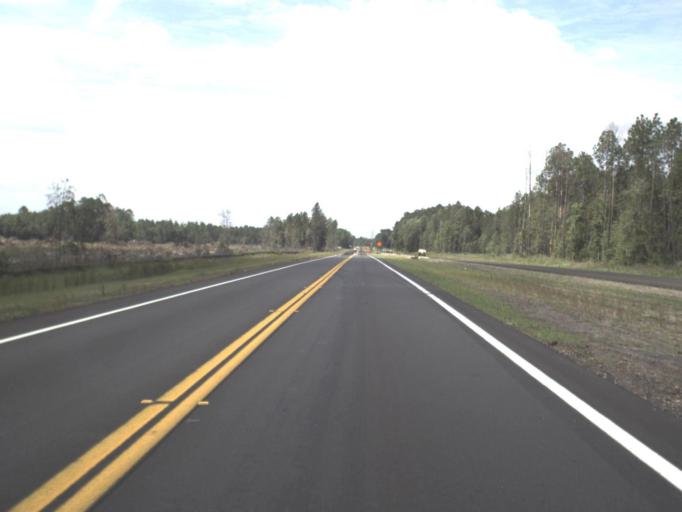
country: US
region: Florida
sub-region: Nassau County
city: Nassau Village-Ratliff
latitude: 30.4889
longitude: -81.8928
